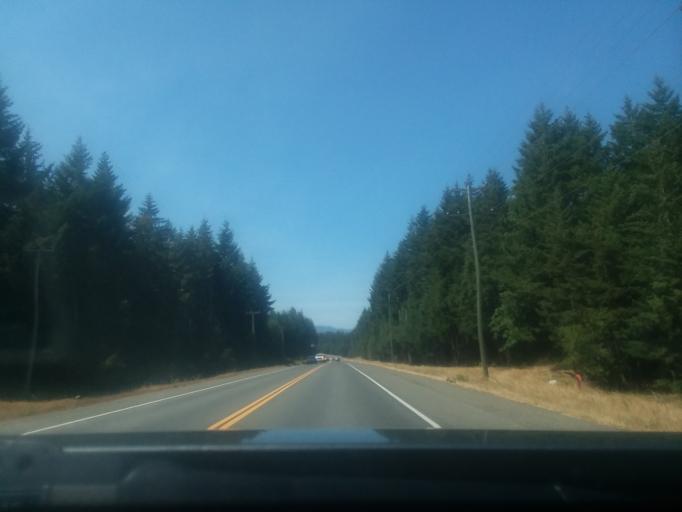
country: CA
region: British Columbia
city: Courtenay
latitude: 49.7152
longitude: -124.9446
